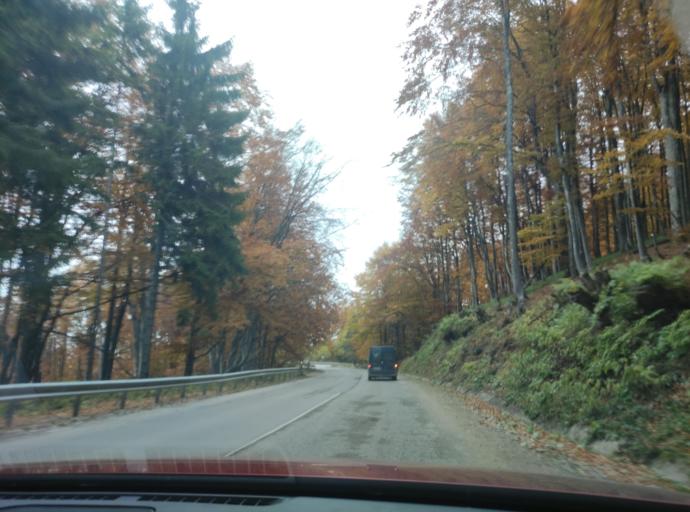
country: BG
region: Montana
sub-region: Obshtina Berkovitsa
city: Berkovitsa
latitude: 43.1239
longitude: 23.1333
